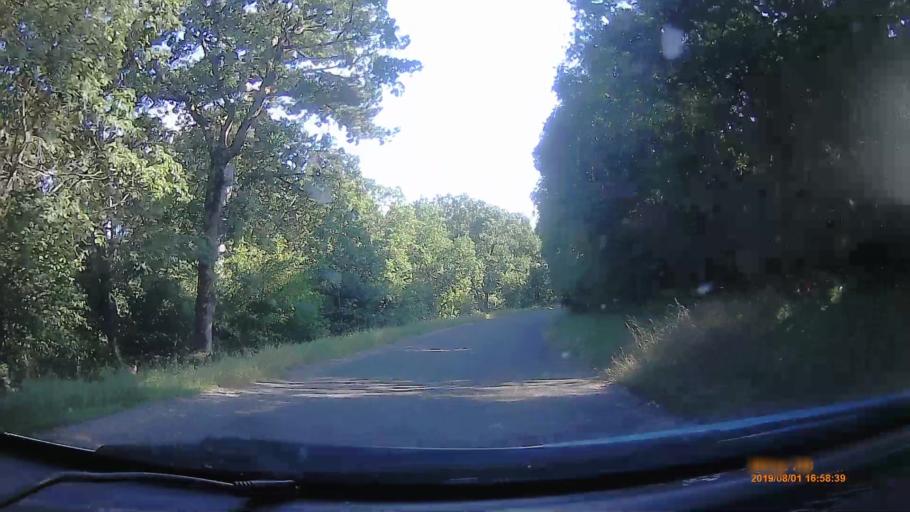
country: HU
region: Baranya
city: Pecs
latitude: 46.0962
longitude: 18.2276
